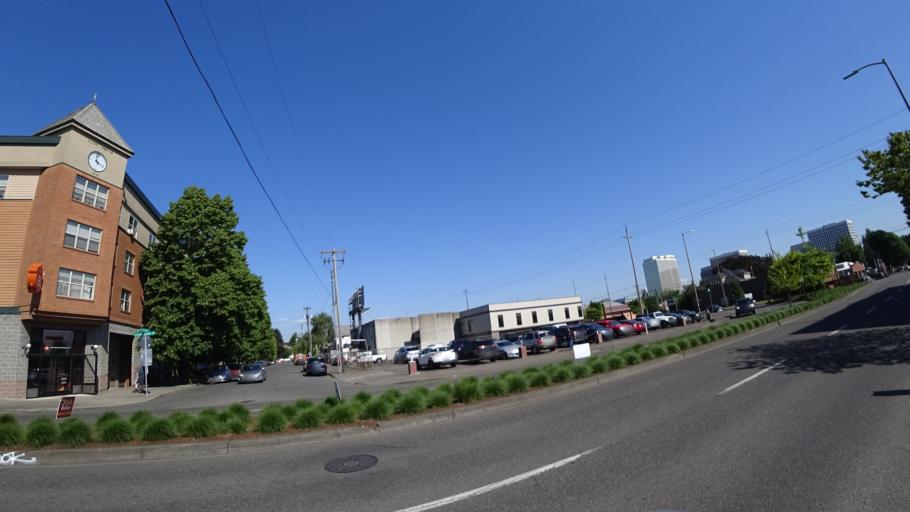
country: US
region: Oregon
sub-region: Multnomah County
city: Portland
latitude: 45.5371
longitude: -122.6618
